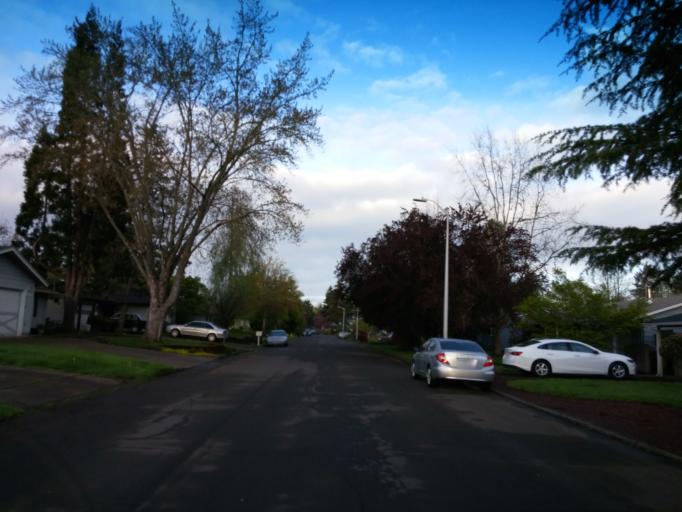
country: US
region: Oregon
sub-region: Washington County
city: Cedar Mill
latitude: 45.5095
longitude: -122.8168
